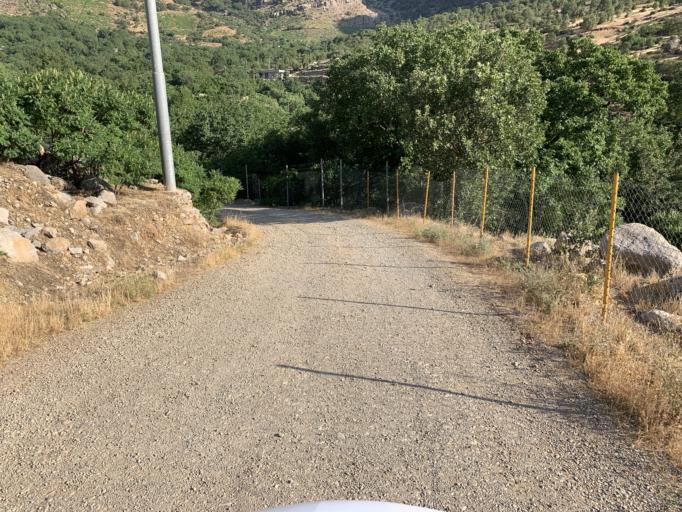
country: IQ
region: As Sulaymaniyah
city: Qeladize
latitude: 35.9896
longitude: 45.2000
